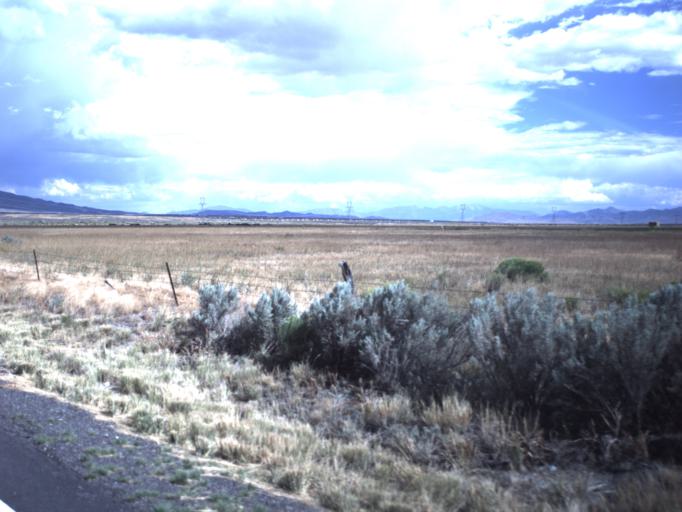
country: US
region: Utah
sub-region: Tooele County
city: Tooele
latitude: 40.3368
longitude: -112.4297
